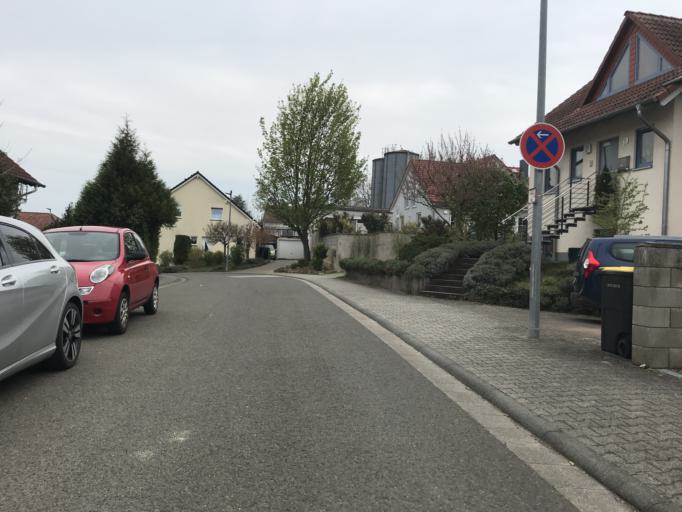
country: DE
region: Rheinland-Pfalz
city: Appenheim
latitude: 49.9333
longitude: 8.0319
